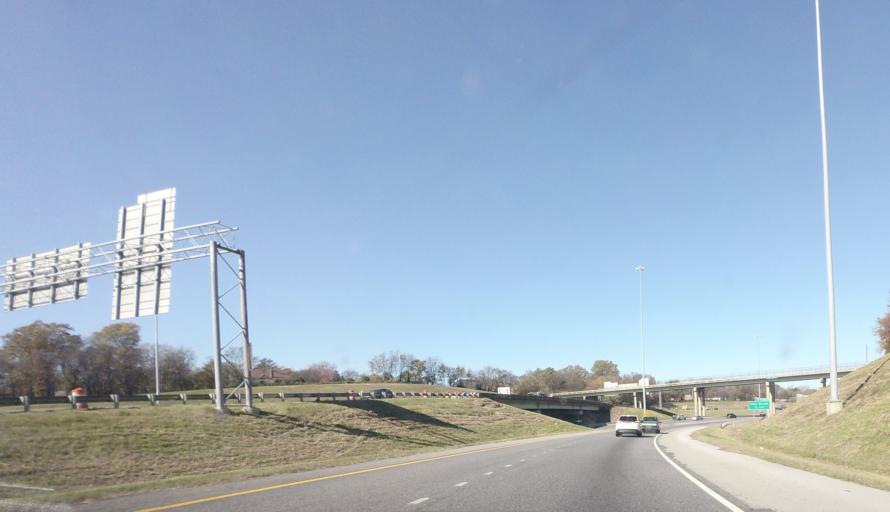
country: US
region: Alabama
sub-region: Jefferson County
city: Birmingham
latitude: 33.5232
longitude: -86.8262
